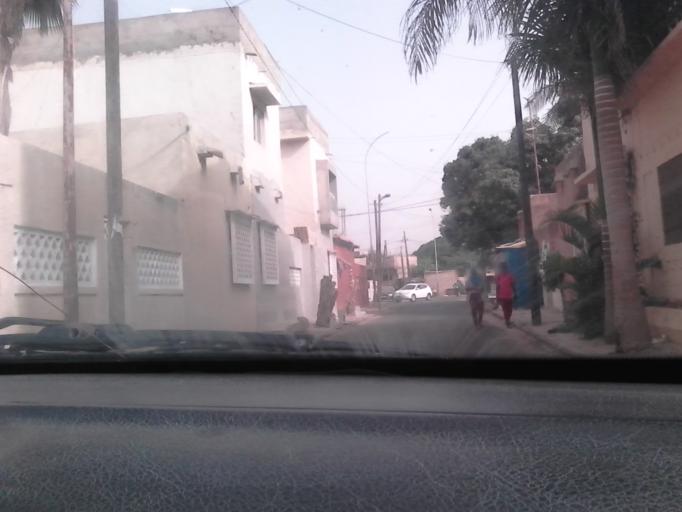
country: SN
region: Dakar
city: Grand Dakar
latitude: 14.7015
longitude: -17.4534
